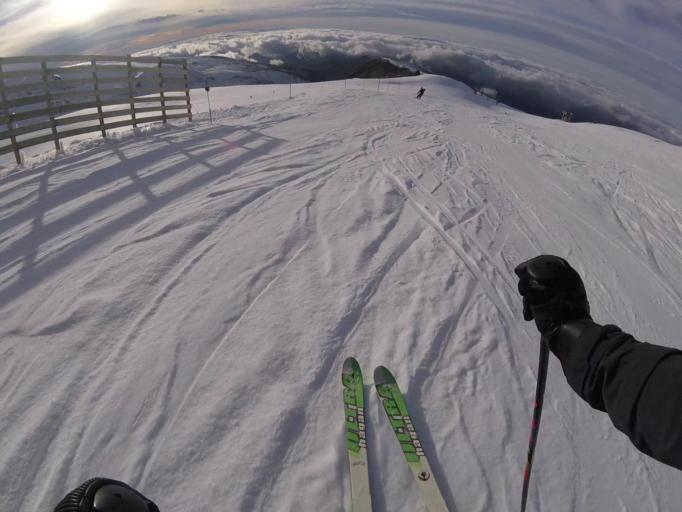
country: ES
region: Andalusia
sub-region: Provincia de Granada
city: Guejar-Sierra
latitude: 37.0709
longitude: -3.4000
